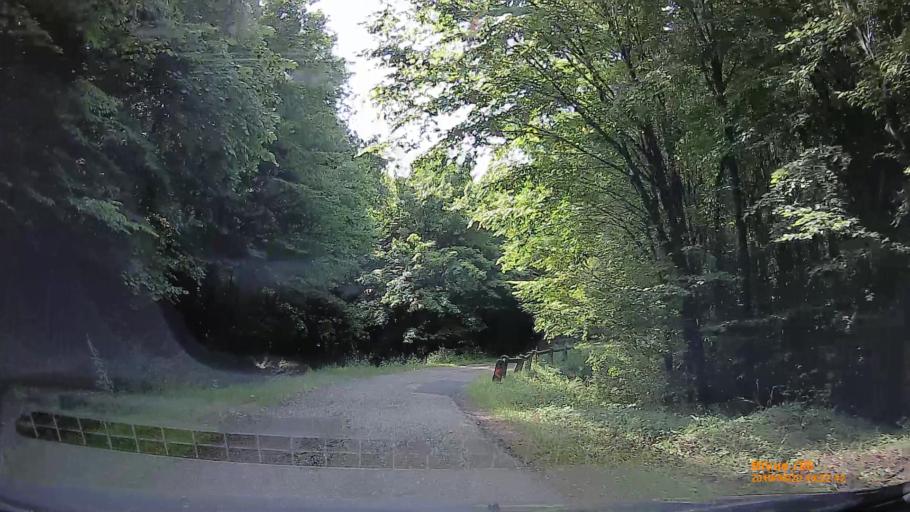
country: HU
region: Baranya
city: Mecseknadasd
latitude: 46.2061
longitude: 18.5158
